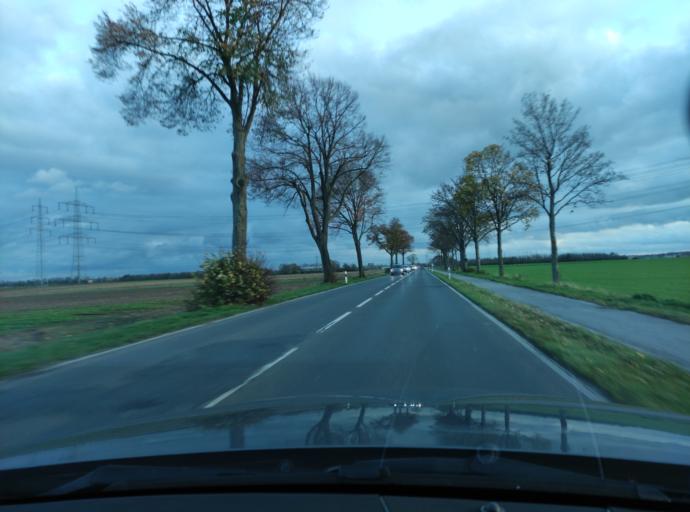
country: DE
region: North Rhine-Westphalia
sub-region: Regierungsbezirk Dusseldorf
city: Dormagen
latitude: 51.1122
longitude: 6.7769
